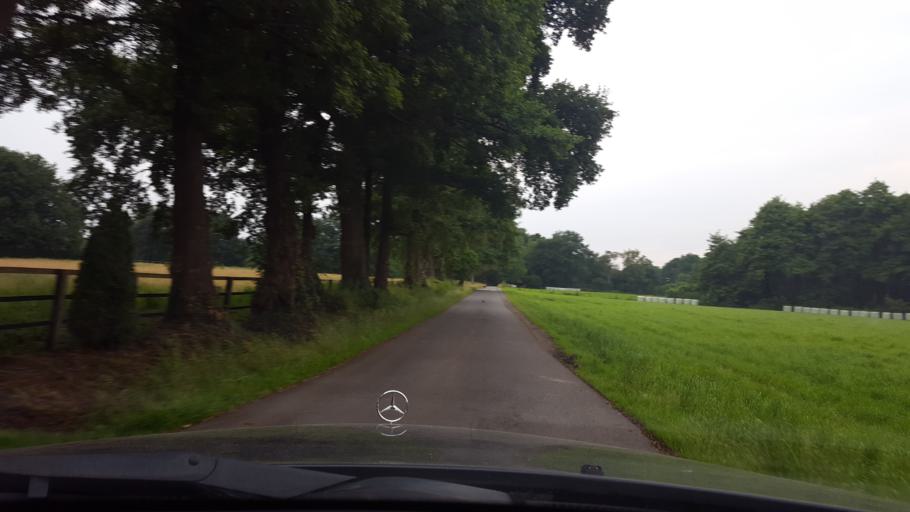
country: DE
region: North Rhine-Westphalia
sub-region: Regierungsbezirk Munster
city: Recklinghausen
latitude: 51.6515
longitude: 7.2125
